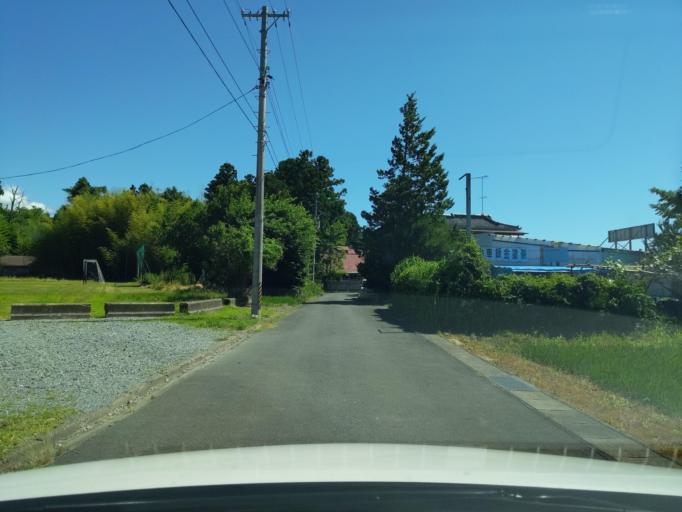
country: JP
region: Fukushima
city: Koriyama
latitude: 37.3780
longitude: 140.2980
